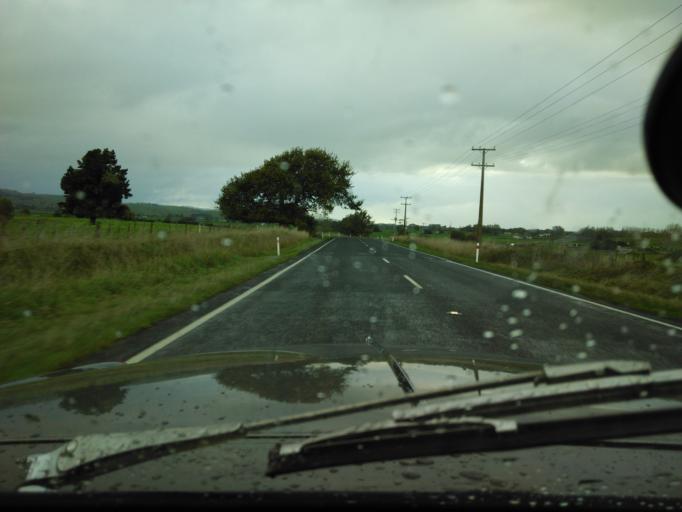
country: NZ
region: Waikato
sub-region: Hauraki District
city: Paeroa
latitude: -37.5837
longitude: 175.5018
